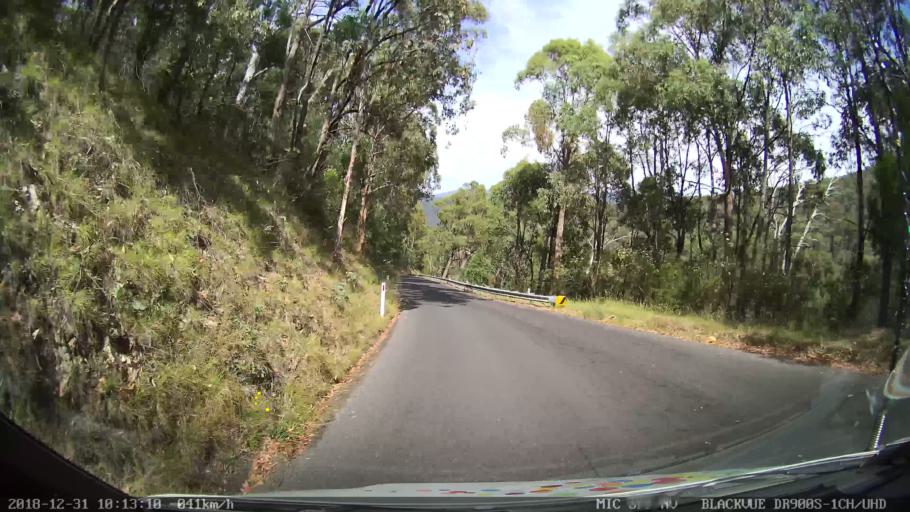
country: AU
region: New South Wales
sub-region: Snowy River
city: Jindabyne
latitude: -36.5376
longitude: 148.1570
